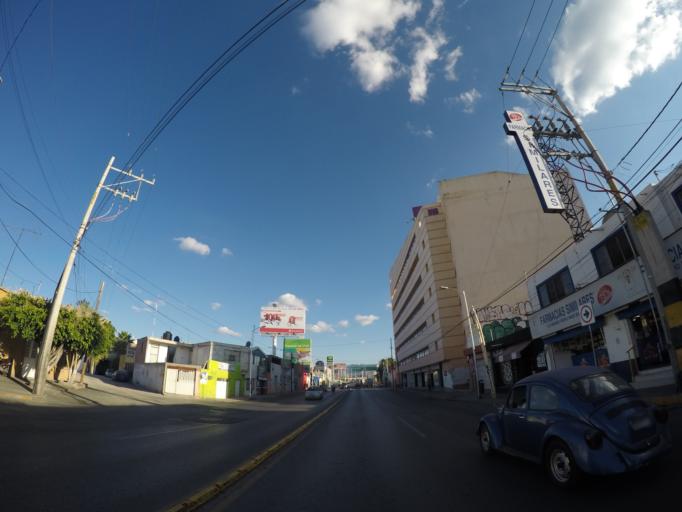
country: MX
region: San Luis Potosi
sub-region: San Luis Potosi
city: San Luis Potosi
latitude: 22.1625
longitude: -101.0007
